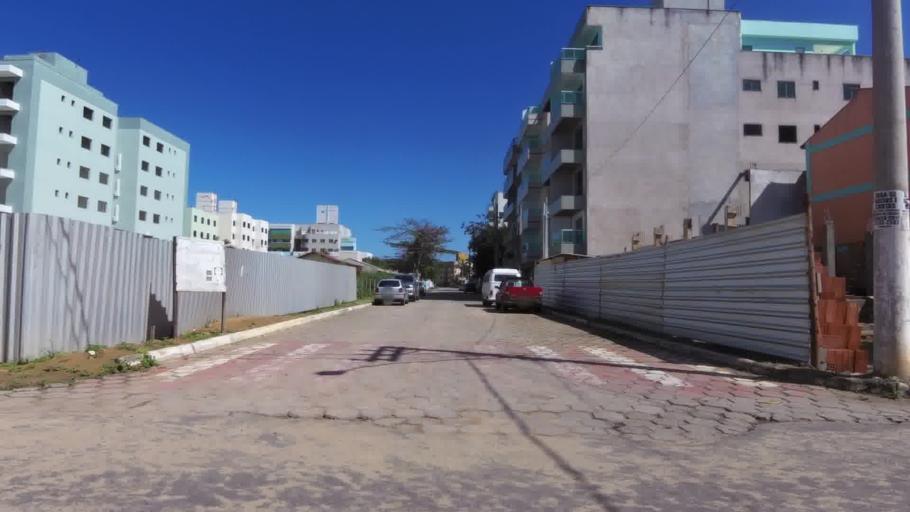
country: BR
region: Espirito Santo
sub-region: Piuma
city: Piuma
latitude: -20.8334
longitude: -40.6231
